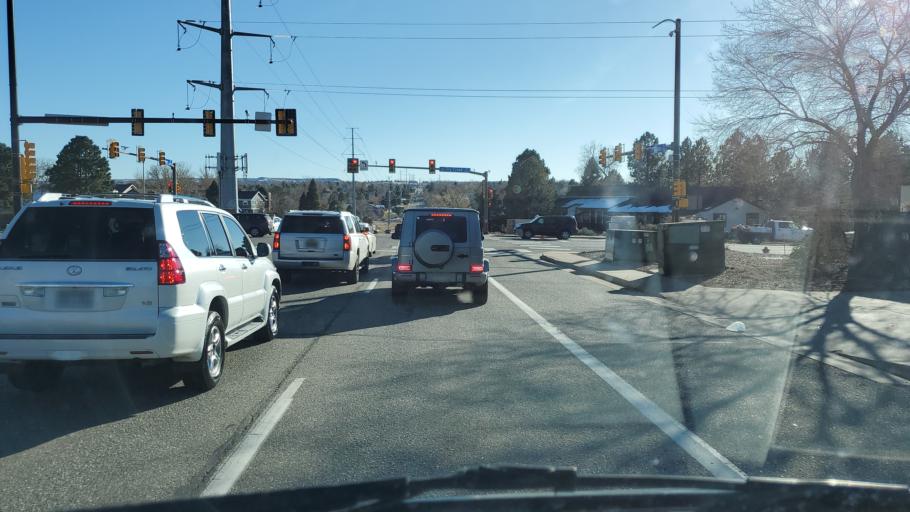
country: US
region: Colorado
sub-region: Arapahoe County
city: Castlewood
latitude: 39.5810
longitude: -104.9043
